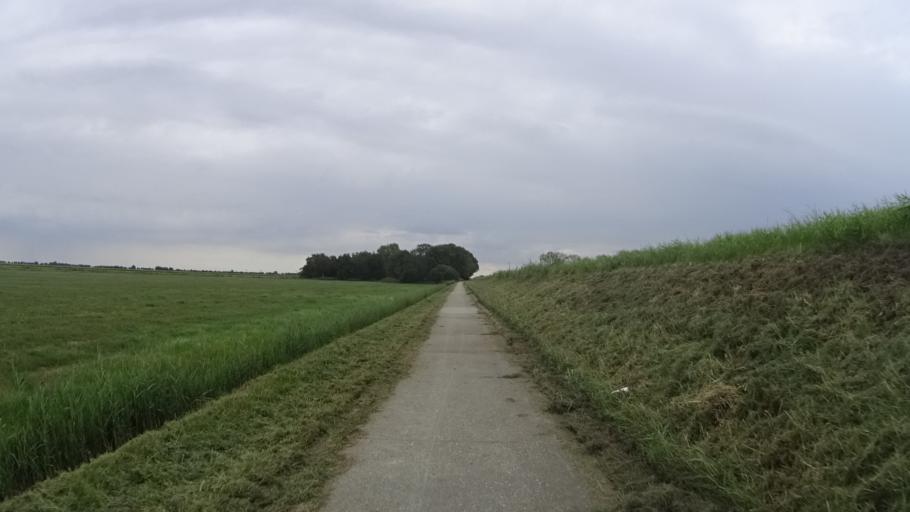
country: NL
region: Groningen
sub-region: Gemeente Haren
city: Haren
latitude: 53.2355
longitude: 6.6871
